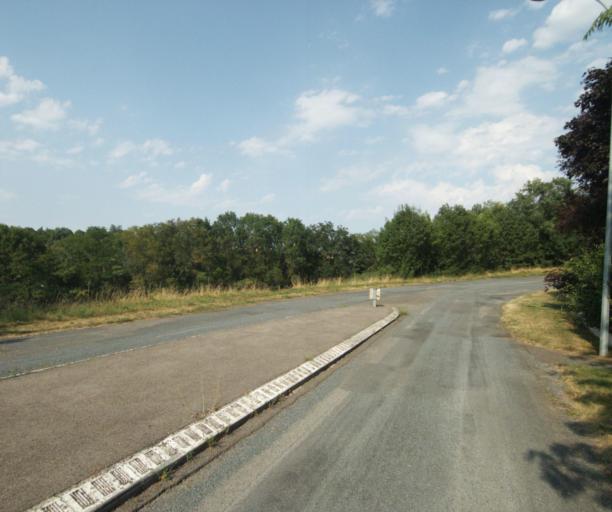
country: FR
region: Rhone-Alpes
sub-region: Departement du Rhone
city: Saint-Germain-Nuelles
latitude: 45.8353
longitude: 4.6051
